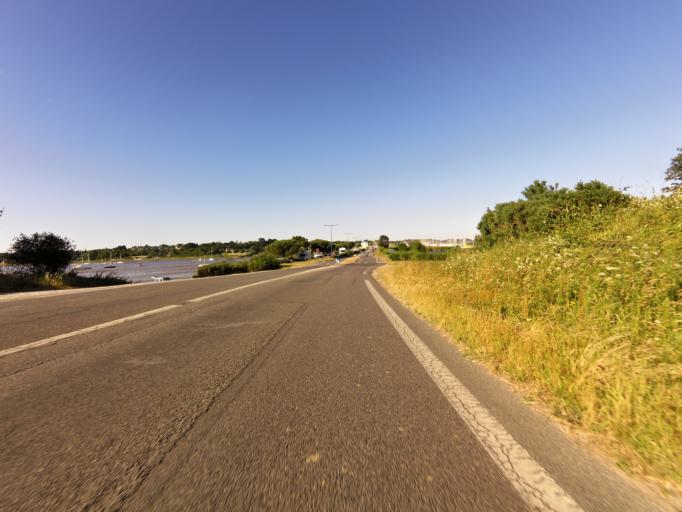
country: FR
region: Brittany
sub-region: Departement du Morbihan
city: Ferel
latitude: 47.4966
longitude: -2.3863
